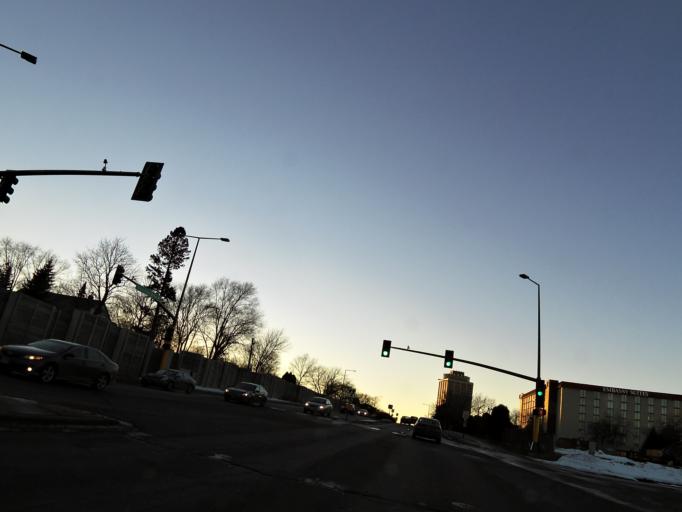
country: US
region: Minnesota
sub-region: Hennepin County
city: Bloomington
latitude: 44.8591
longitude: -93.3133
